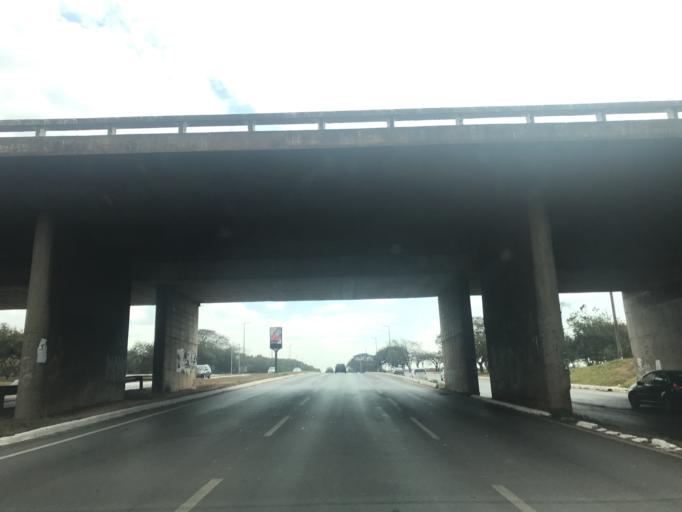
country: BR
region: Federal District
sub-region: Brasilia
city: Brasilia
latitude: -15.8454
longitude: -47.9313
